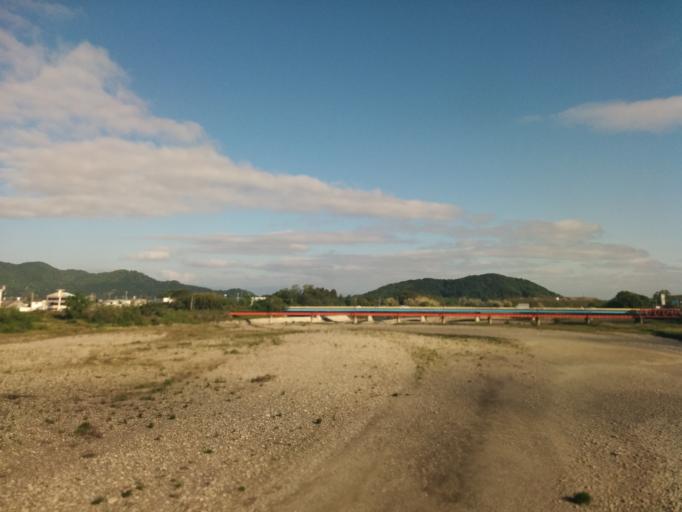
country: JP
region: Shiga Prefecture
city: Youkaichi
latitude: 35.1609
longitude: 136.2022
